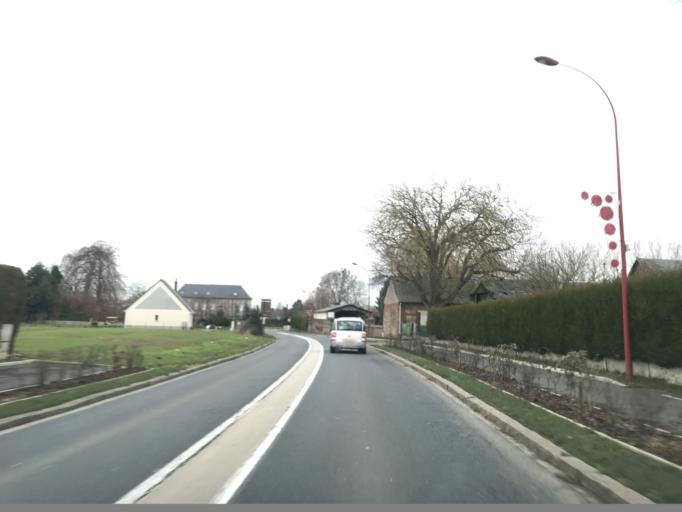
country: FR
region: Haute-Normandie
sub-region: Departement de l'Eure
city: Fleury-sur-Andelle
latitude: 49.3845
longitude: 1.3142
